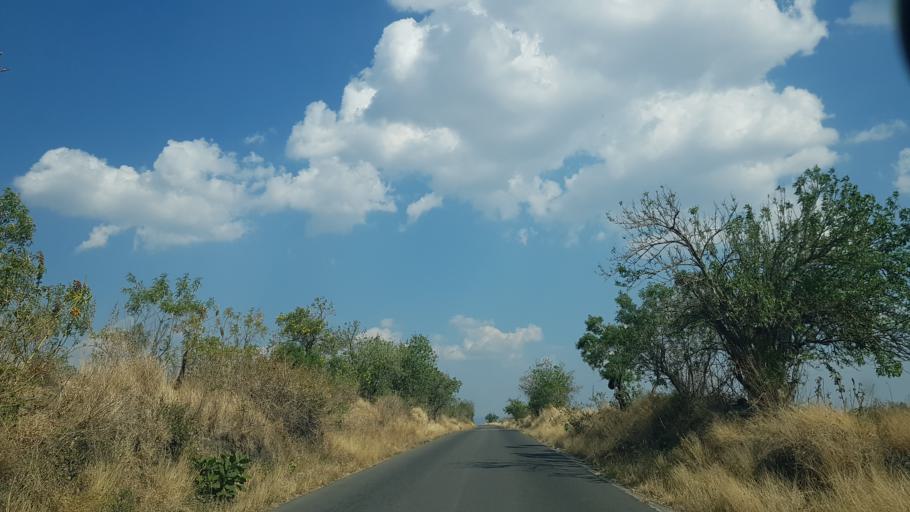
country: MX
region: Puebla
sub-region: Atlixco
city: Colonia Agricola de Ocotepec (Colonia San Jose)
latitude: 18.9198
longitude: -98.5315
